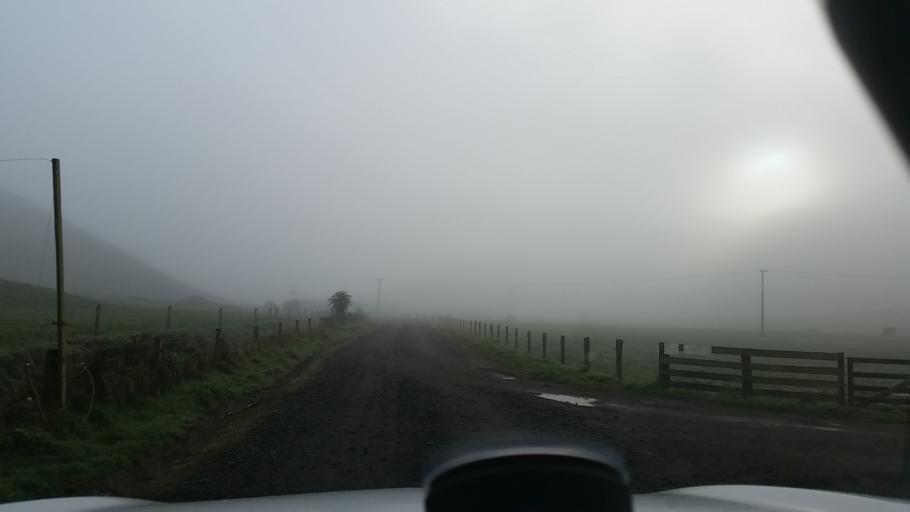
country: NZ
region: Taranaki
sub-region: South Taranaki District
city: Eltham
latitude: -39.4075
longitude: 174.4303
